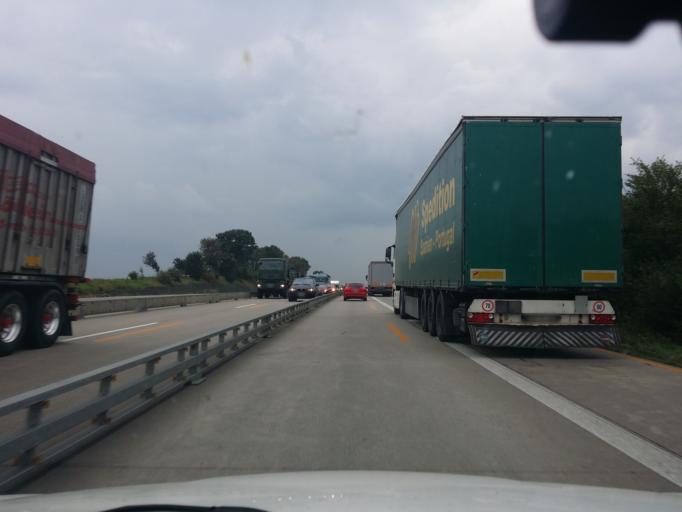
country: DE
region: Saxony-Anhalt
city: Osterfeld
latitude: 51.0745
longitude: 11.9553
